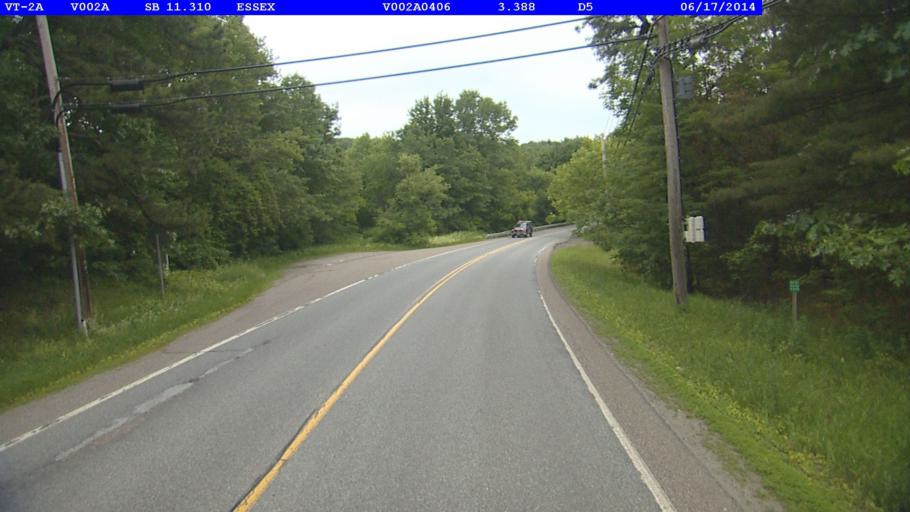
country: US
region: Vermont
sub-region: Chittenden County
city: Colchester
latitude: 44.5275
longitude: -73.1272
